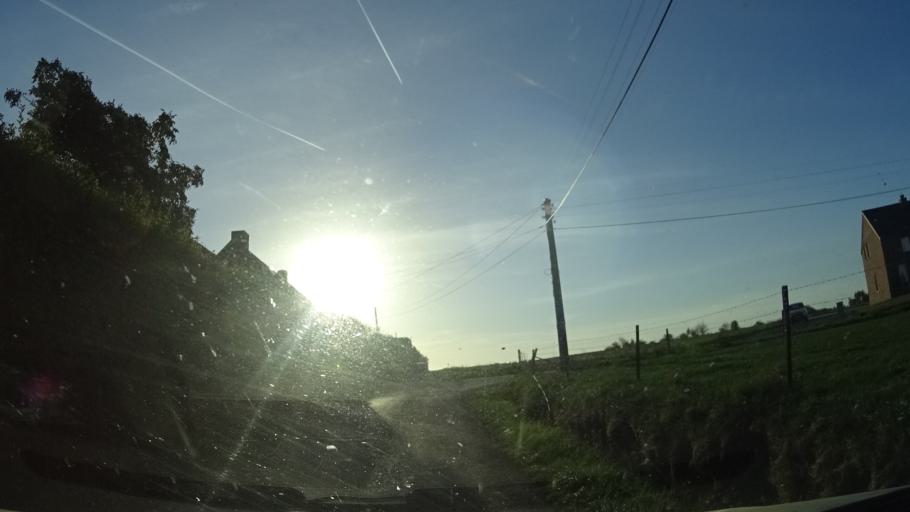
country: BE
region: Wallonia
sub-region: Province du Hainaut
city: Beaumont
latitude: 50.2575
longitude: 4.2437
